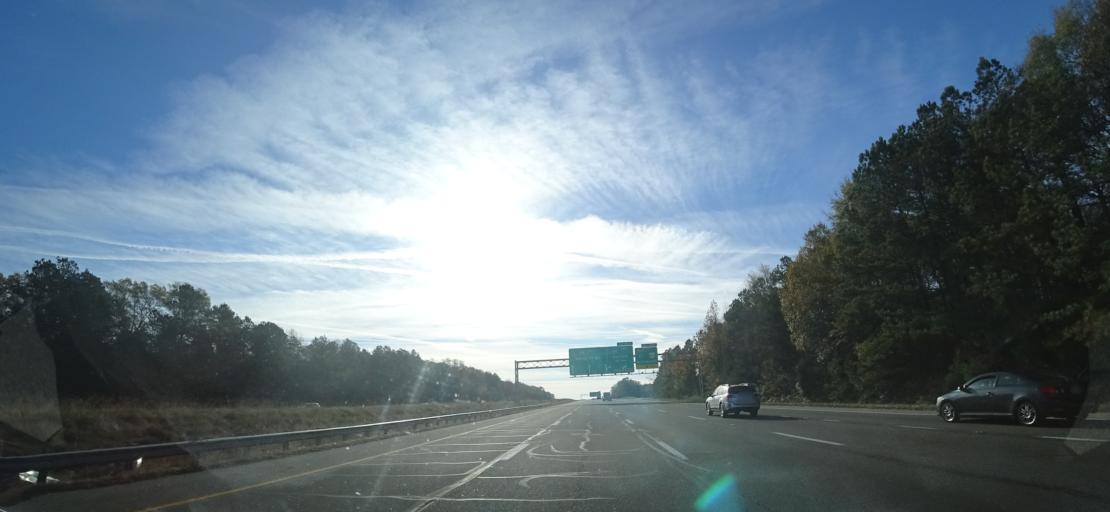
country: US
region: Virginia
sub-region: Henrico County
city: Sandston
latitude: 37.5380
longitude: -77.2788
